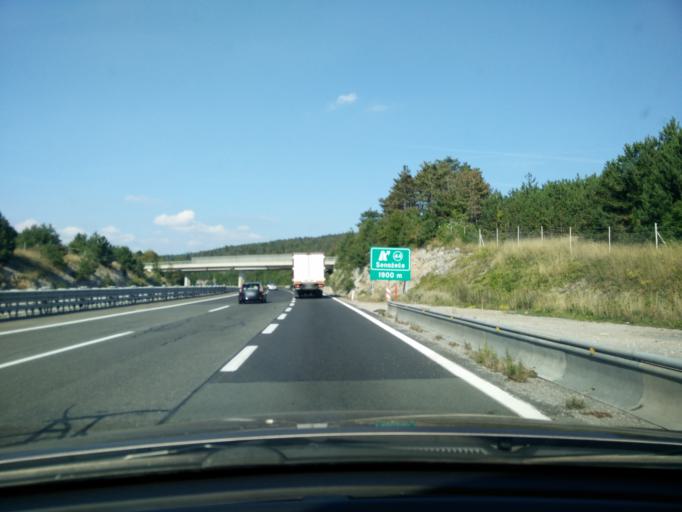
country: SI
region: Divaca
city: Divaca
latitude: 45.7048
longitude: 13.9997
